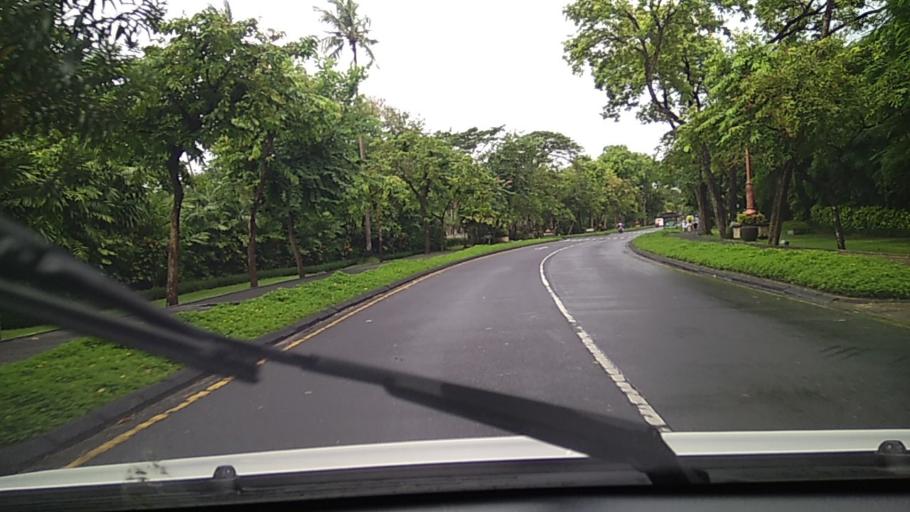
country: ID
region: Bali
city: Bualu
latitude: -8.7907
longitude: 115.2272
